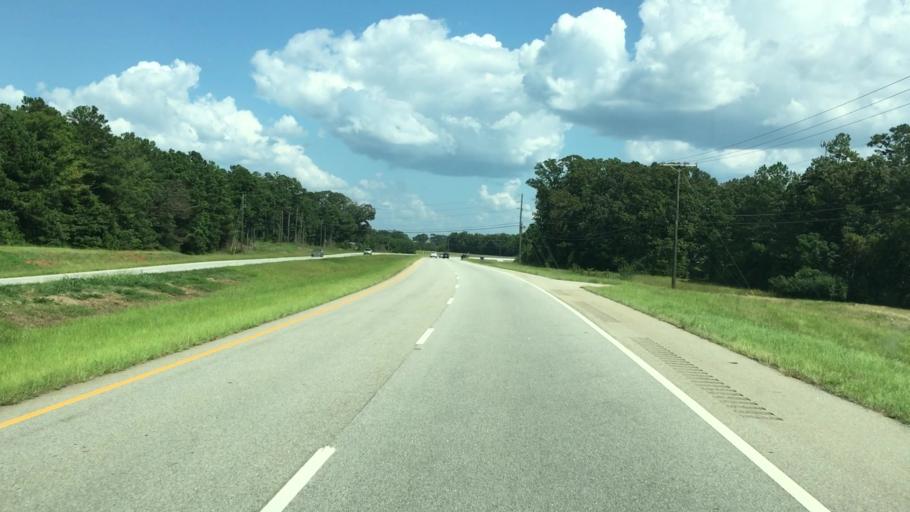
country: US
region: Georgia
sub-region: Putnam County
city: Eatonton
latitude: 33.2700
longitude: -83.3424
